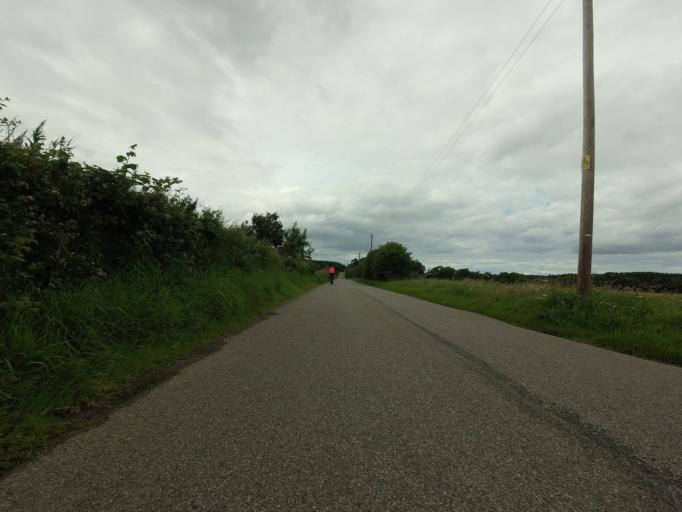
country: GB
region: Scotland
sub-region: Moray
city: Forres
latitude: 57.5977
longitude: -3.7180
